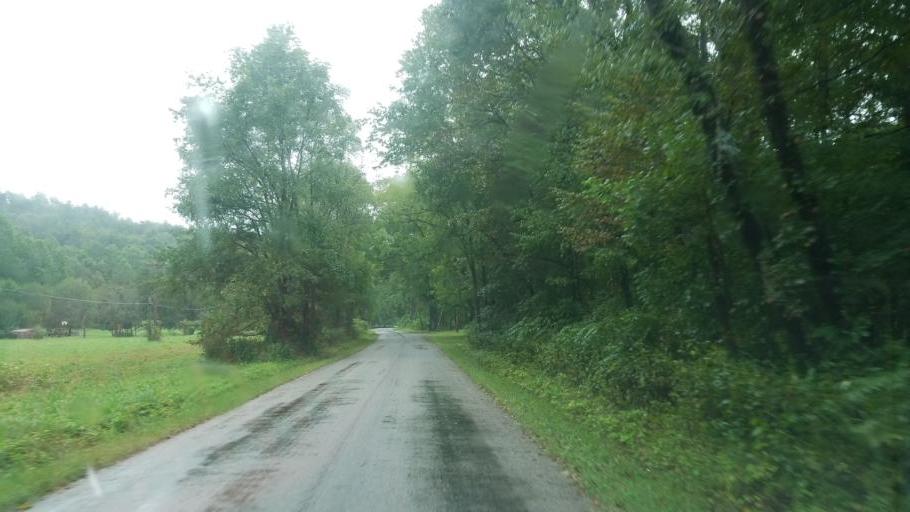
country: US
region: Ohio
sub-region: Adams County
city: Peebles
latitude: 38.8120
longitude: -83.2422
